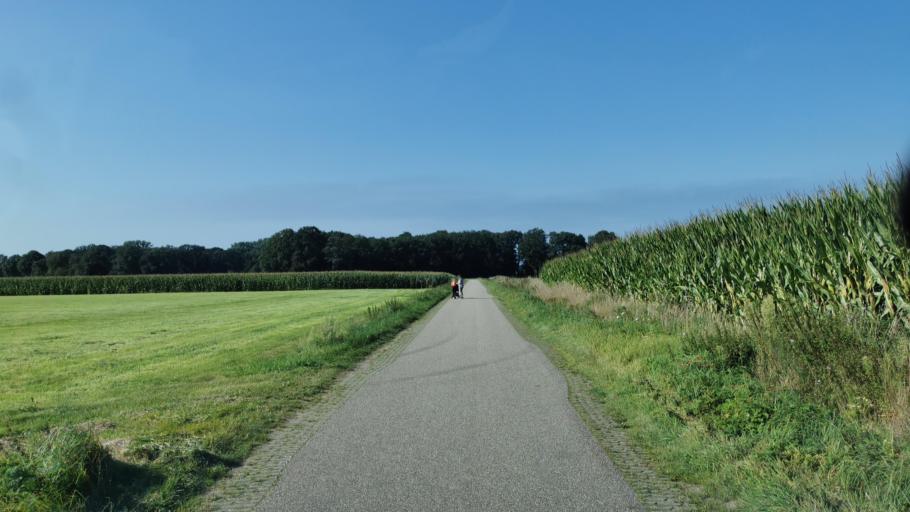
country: DE
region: Lower Saxony
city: Lage
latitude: 52.4006
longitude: 6.9482
